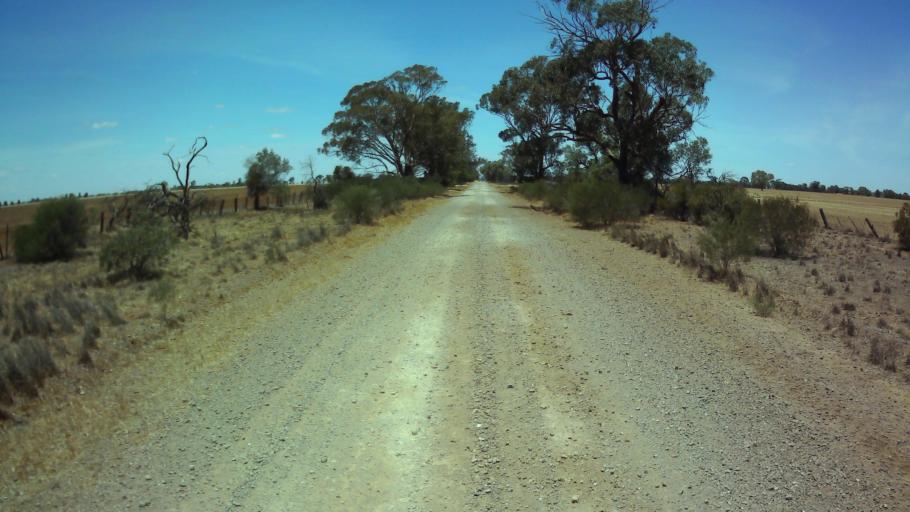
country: AU
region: New South Wales
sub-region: Weddin
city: Grenfell
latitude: -33.9419
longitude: 147.7116
